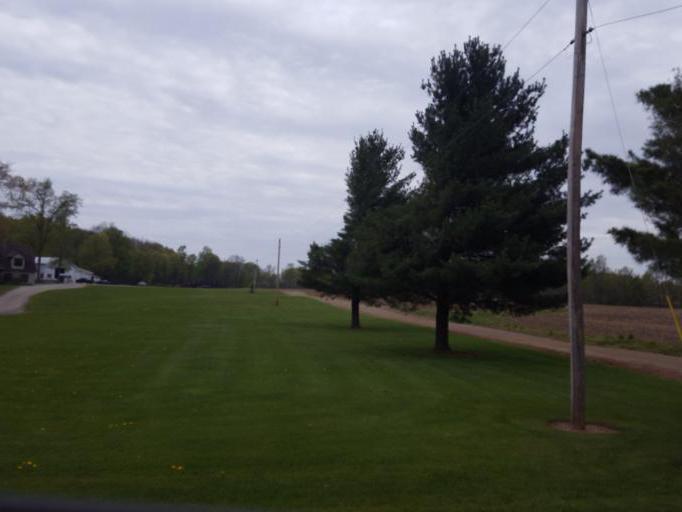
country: US
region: Ohio
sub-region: Richland County
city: Lexington
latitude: 40.6938
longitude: -82.6460
